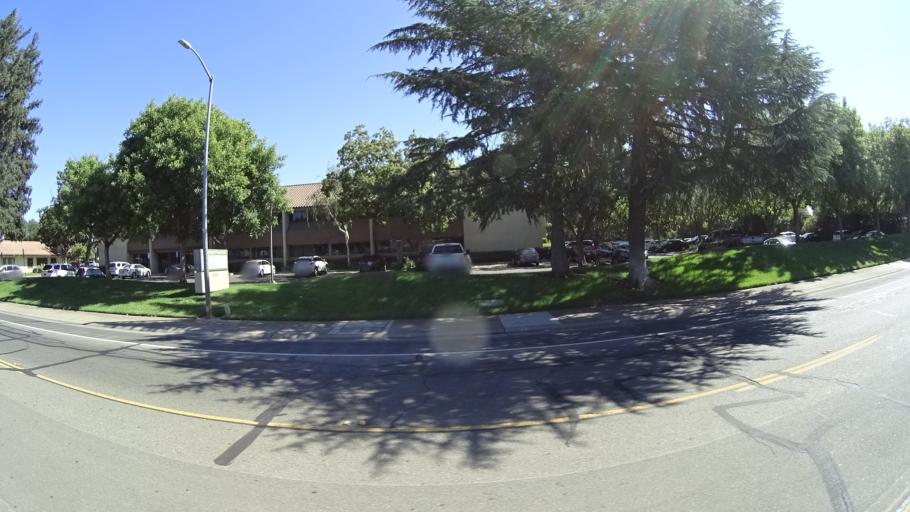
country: US
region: California
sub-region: Sacramento County
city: Elk Grove
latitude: 38.4045
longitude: -121.3715
